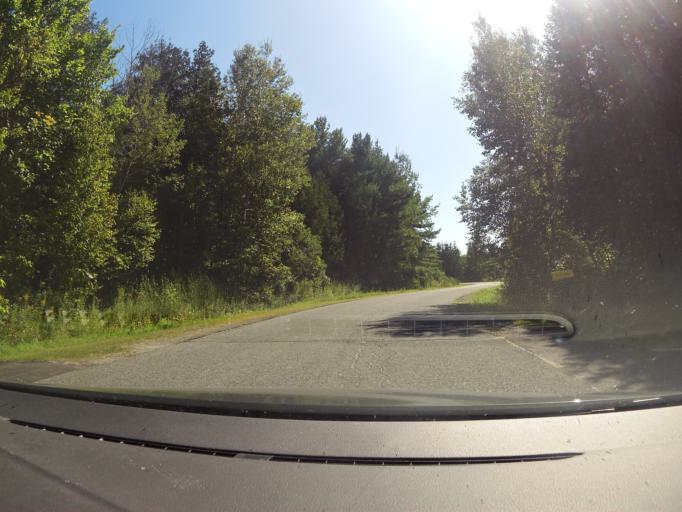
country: CA
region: Ontario
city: Bells Corners
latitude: 45.2756
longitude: -76.0117
